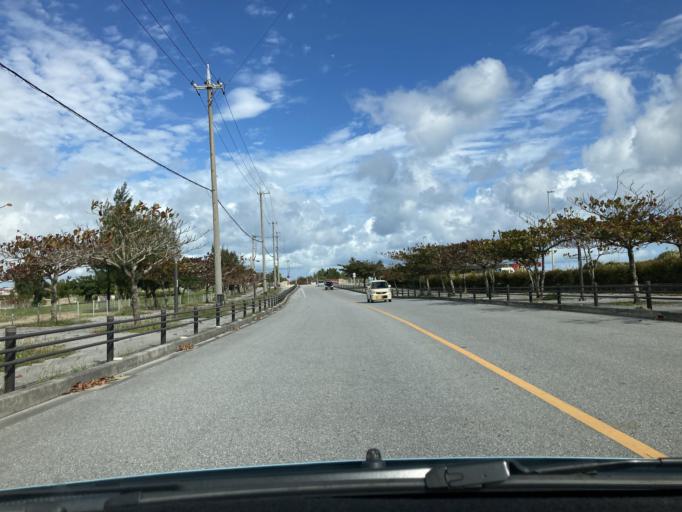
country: JP
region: Okinawa
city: Ginowan
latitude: 26.2136
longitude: 127.7725
